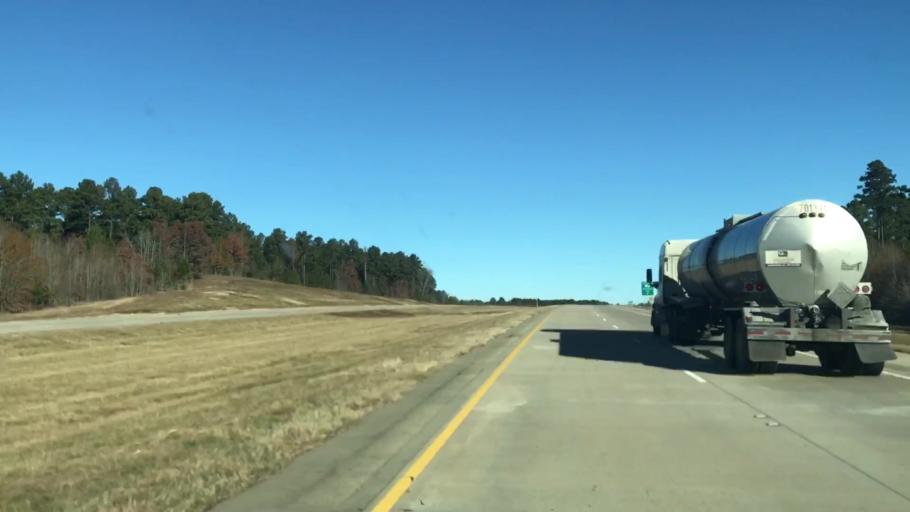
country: US
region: Louisiana
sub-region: Caddo Parish
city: Vivian
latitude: 32.9890
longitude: -93.9105
